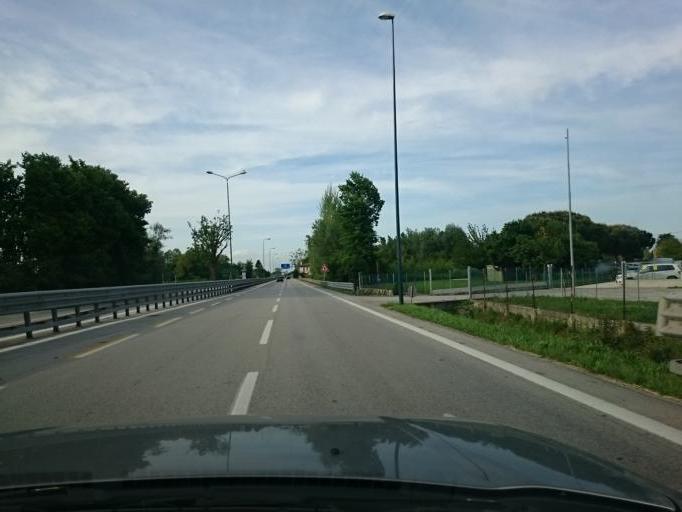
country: IT
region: Veneto
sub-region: Provincia di Venezia
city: Campalto
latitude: 45.4875
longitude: 12.2742
